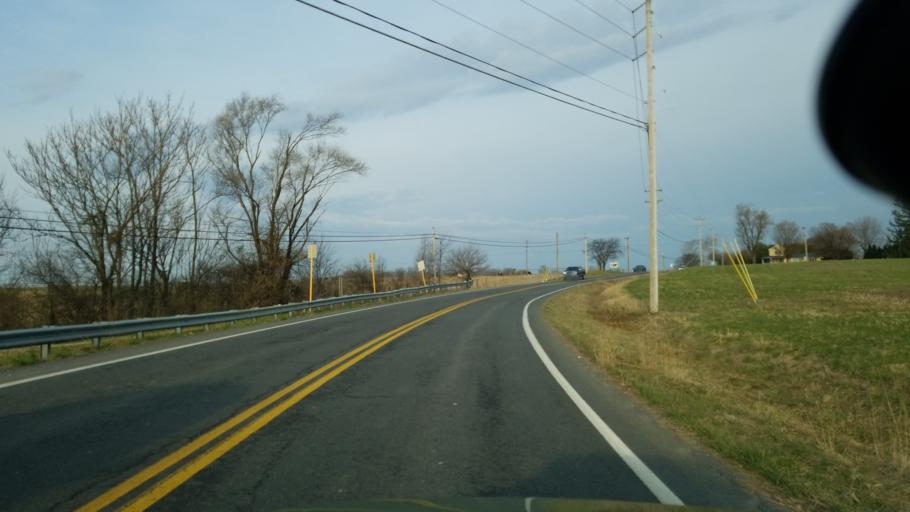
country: US
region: Virginia
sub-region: Clarke County
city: Berryville
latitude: 39.1450
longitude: -77.9611
